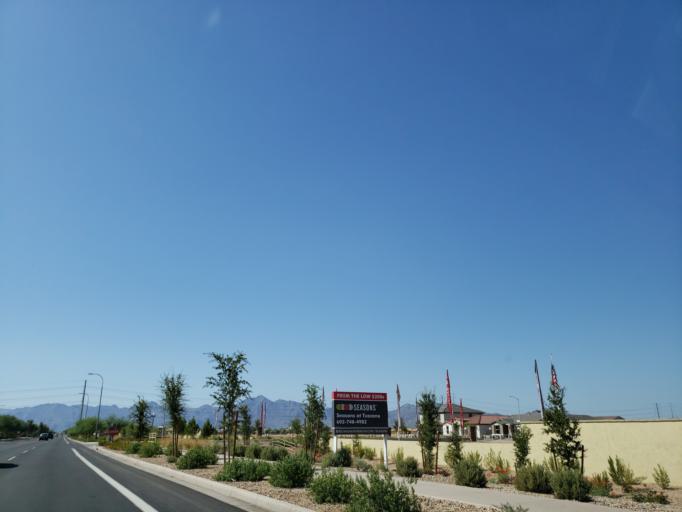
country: US
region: Arizona
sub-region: Maricopa County
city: Tolleson
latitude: 33.4196
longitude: -112.2213
